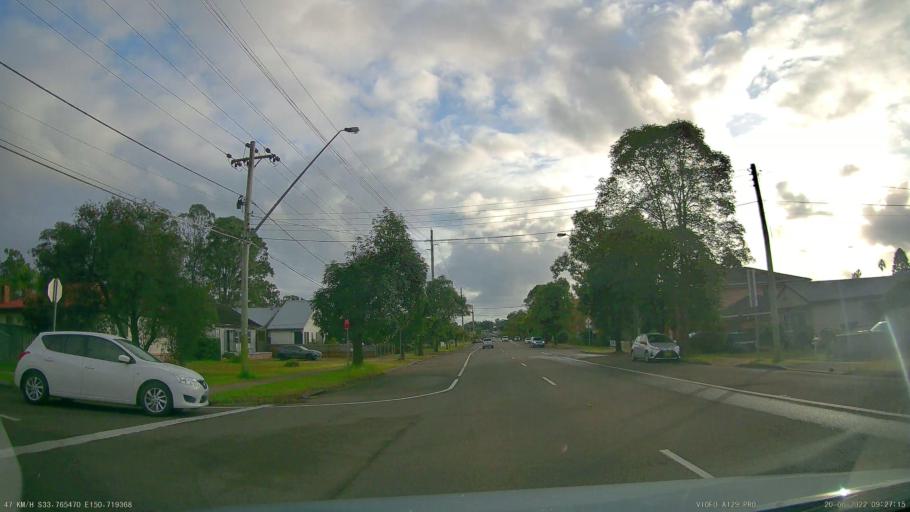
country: AU
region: New South Wales
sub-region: Penrith Municipality
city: Kingswood Park
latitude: -33.7652
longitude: 150.7194
